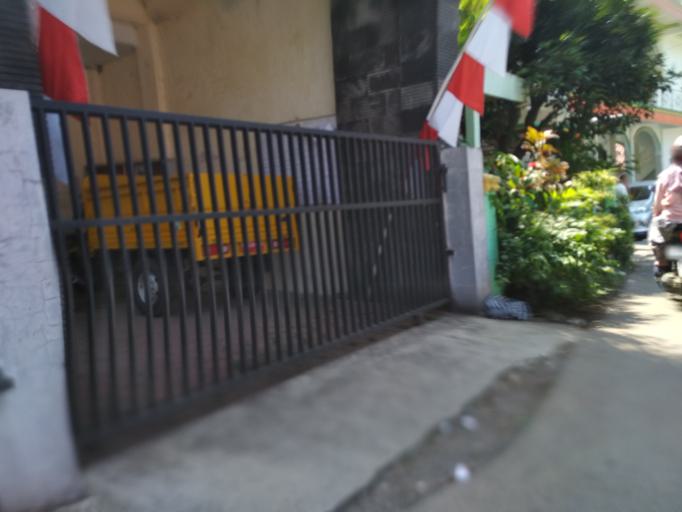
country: ID
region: West Java
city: Ciampea
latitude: -6.5601
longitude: 106.7416
